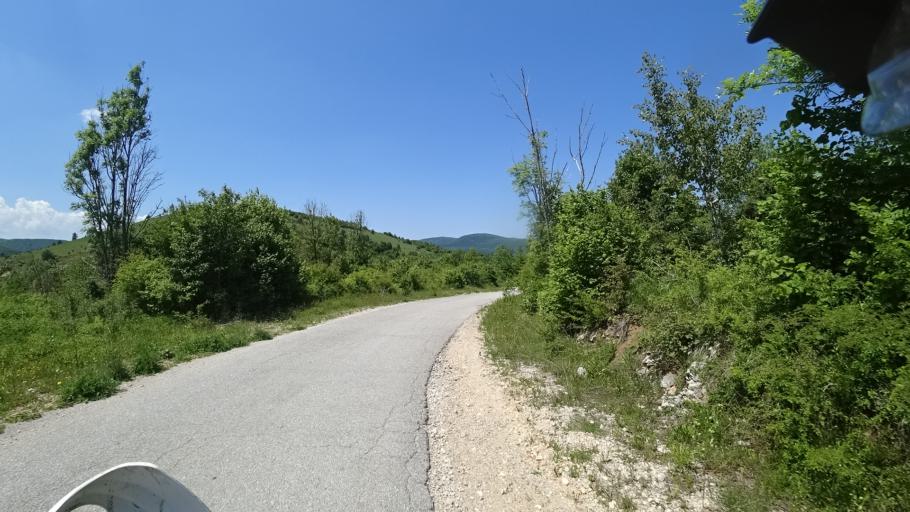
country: HR
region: Karlovacka
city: Plaski
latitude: 44.9557
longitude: 15.3423
